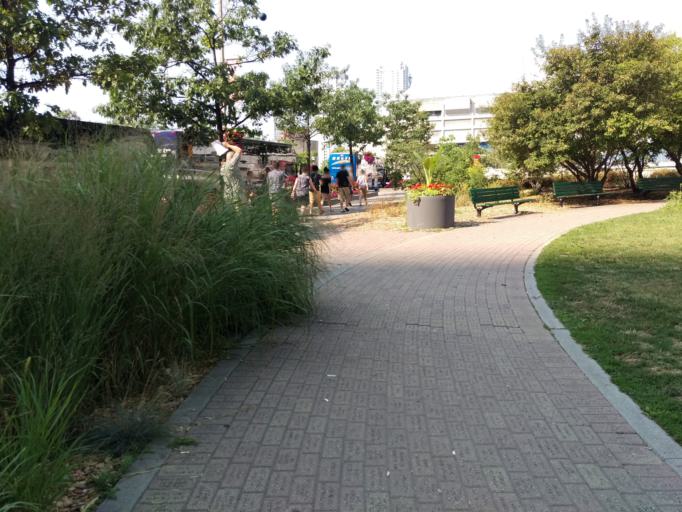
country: CA
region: Ontario
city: Toronto
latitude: 43.6425
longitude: -79.3844
